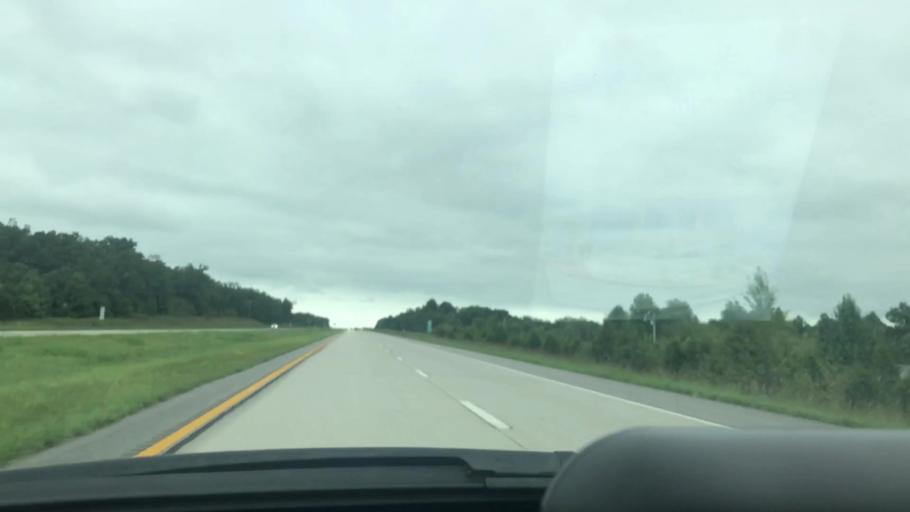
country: US
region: Missouri
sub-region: Greene County
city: Fair Grove
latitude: 37.4705
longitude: -93.1396
